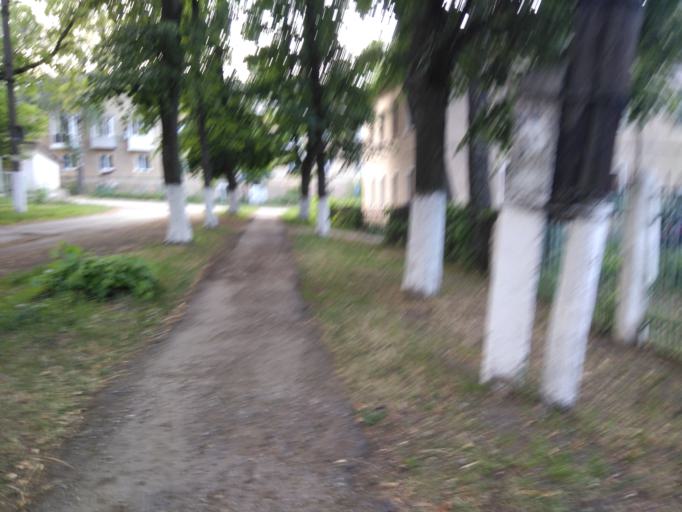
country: RU
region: Tula
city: Lomintsevskiy
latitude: 53.9346
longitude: 37.6260
